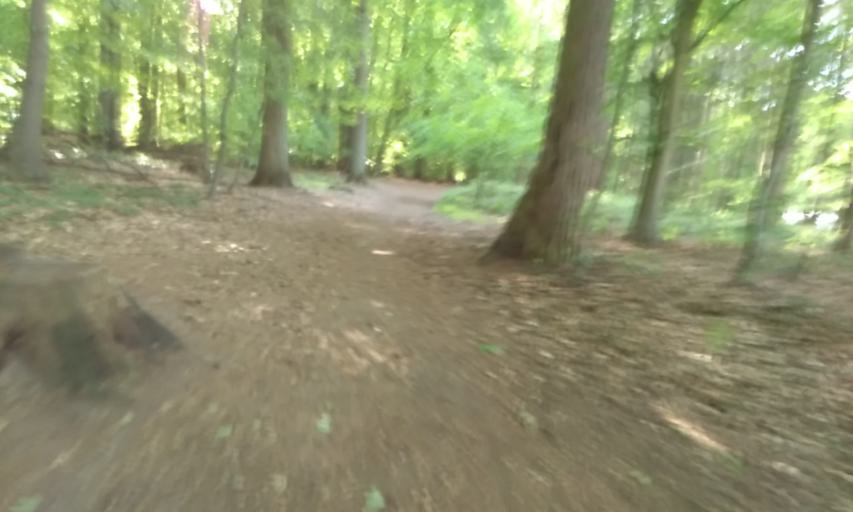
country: DE
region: Lower Saxony
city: Buxtehude
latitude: 53.4698
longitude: 9.6700
